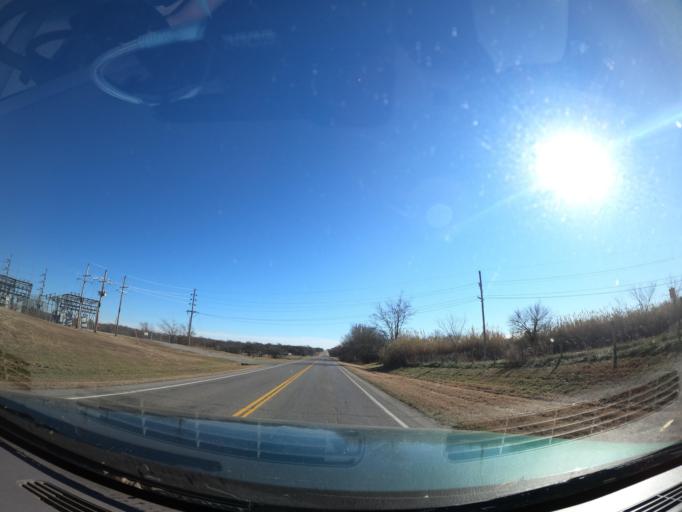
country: US
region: Oklahoma
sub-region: Muskogee County
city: Haskell
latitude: 35.7772
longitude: -95.6588
